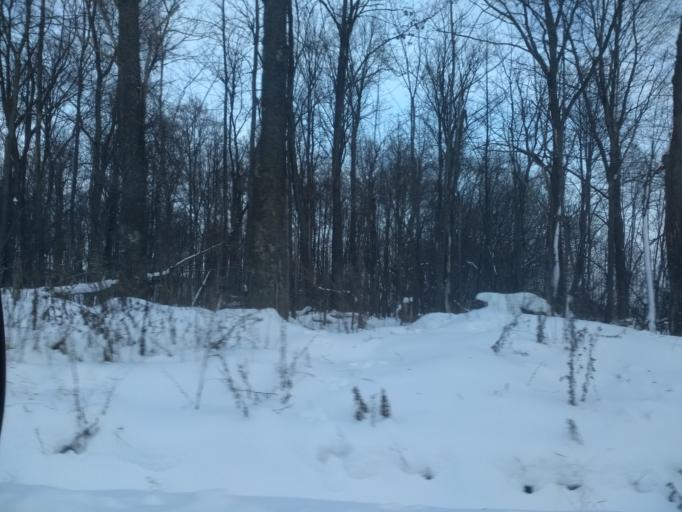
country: RU
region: Bashkortostan
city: Kudeyevskiy
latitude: 54.7159
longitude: 56.6136
